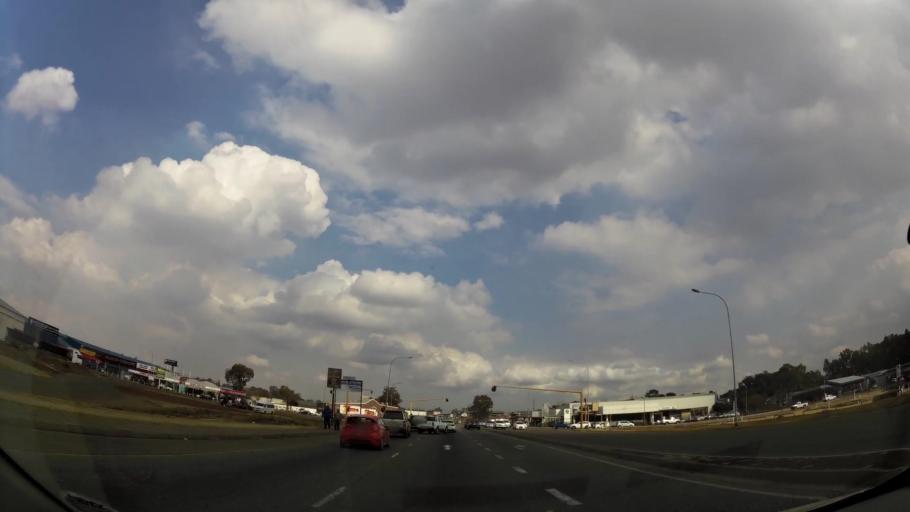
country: ZA
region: Gauteng
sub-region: Sedibeng District Municipality
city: Vereeniging
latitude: -26.6614
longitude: 27.9347
